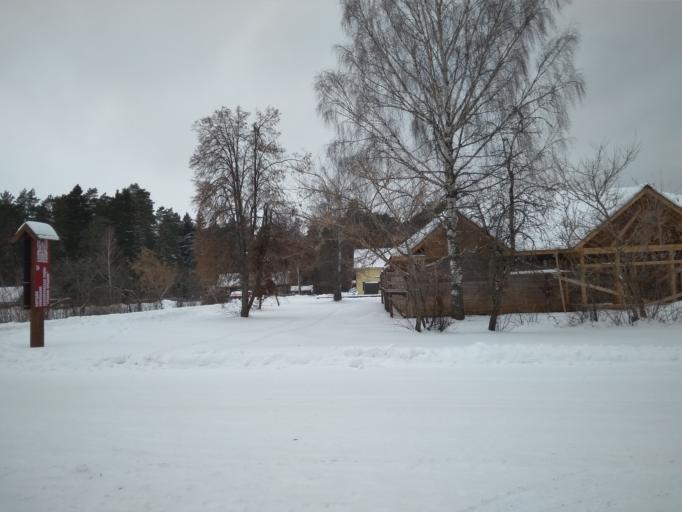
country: RU
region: Mordoviya
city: Sosnovka
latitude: 54.7131
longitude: 43.2263
